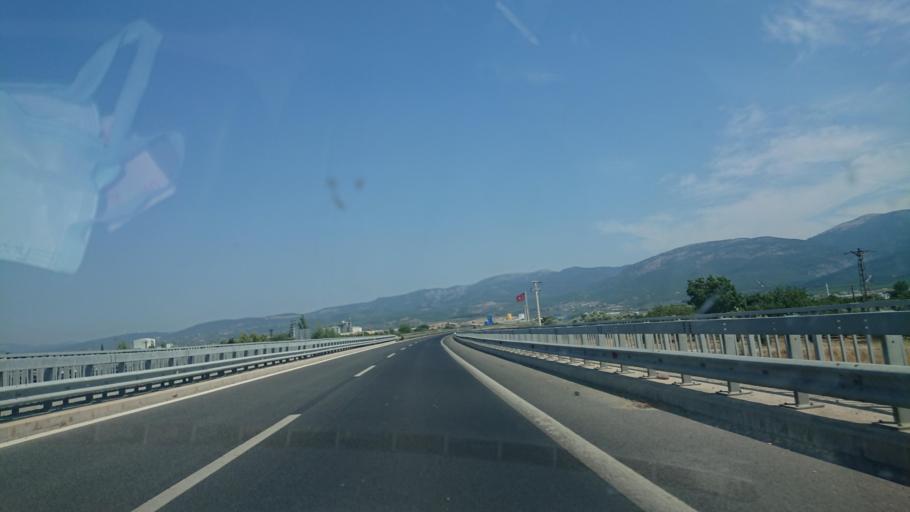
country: TR
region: Izmir
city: Kemalpasa
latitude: 38.4451
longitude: 27.4318
